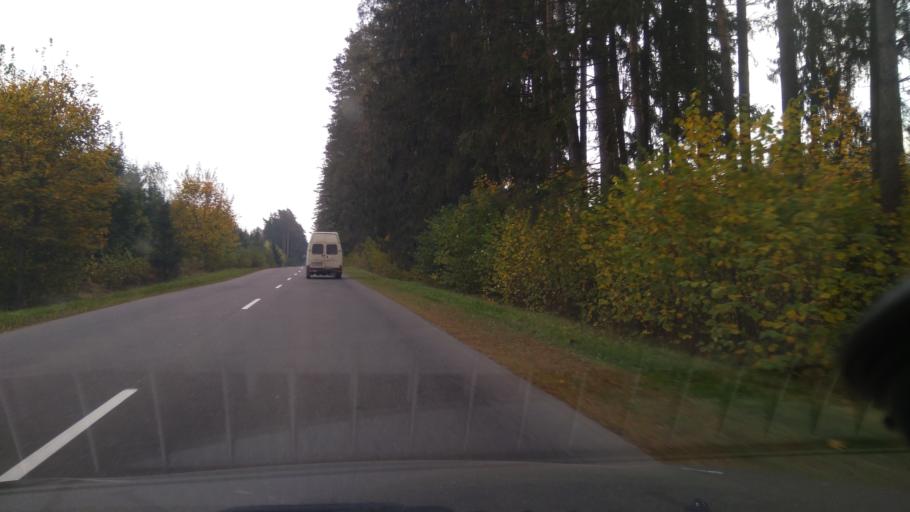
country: BY
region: Minsk
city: Rudzyensk
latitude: 53.6139
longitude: 27.7738
